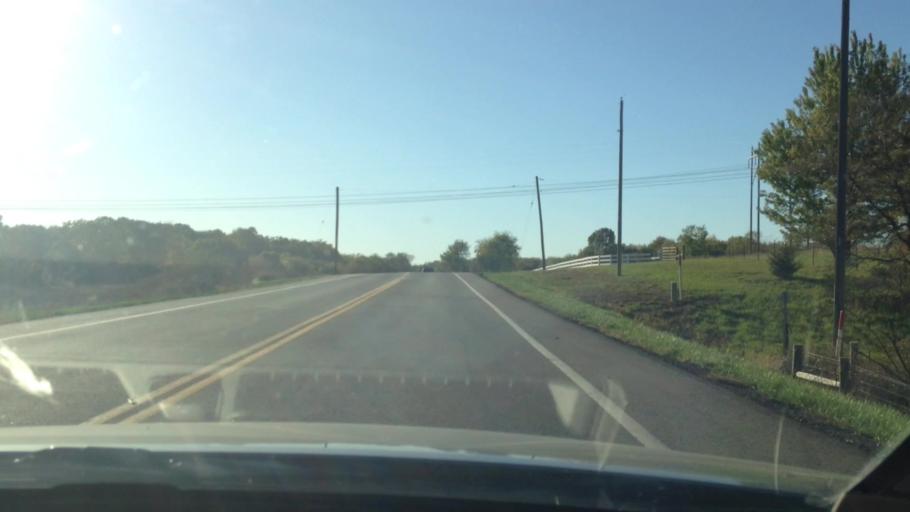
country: US
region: Kansas
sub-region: Johnson County
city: Edgerton
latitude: 38.7677
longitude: -94.9848
